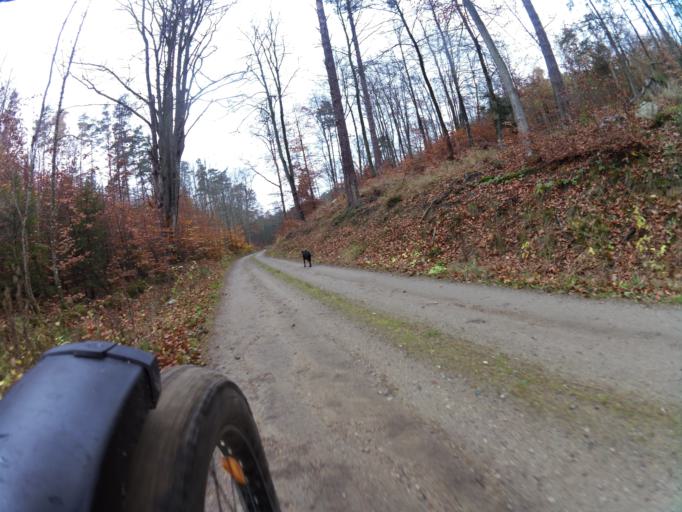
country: PL
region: Pomeranian Voivodeship
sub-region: Powiat pucki
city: Krokowa
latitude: 54.7136
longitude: 18.1415
